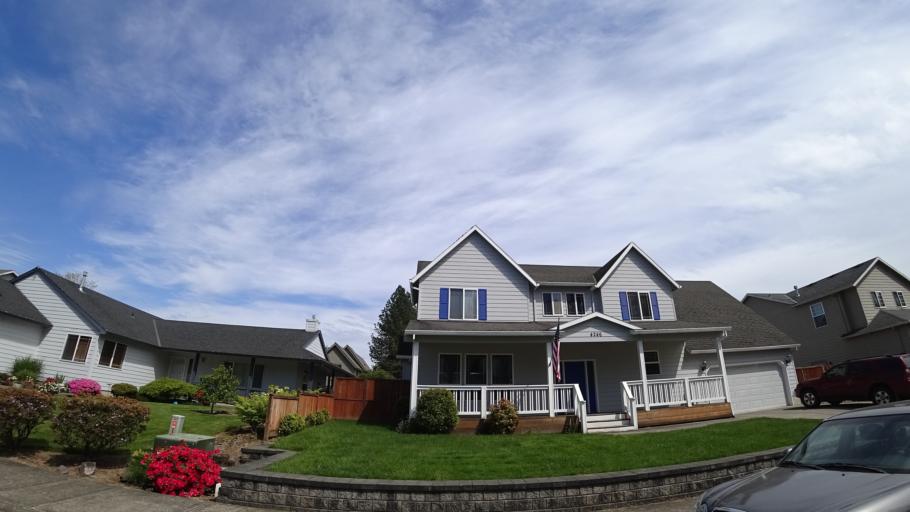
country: US
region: Oregon
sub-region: Washington County
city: Aloha
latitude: 45.4886
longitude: -122.8870
